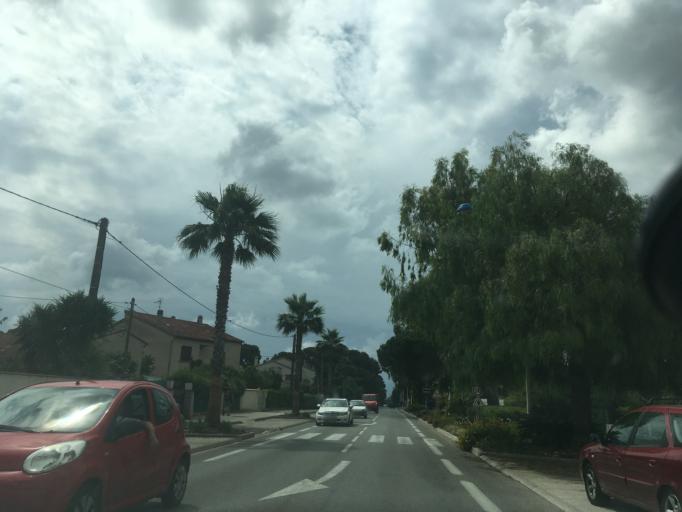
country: FR
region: Provence-Alpes-Cote d'Azur
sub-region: Departement du Var
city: La Londe-les-Maures
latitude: 43.1339
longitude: 6.2376
